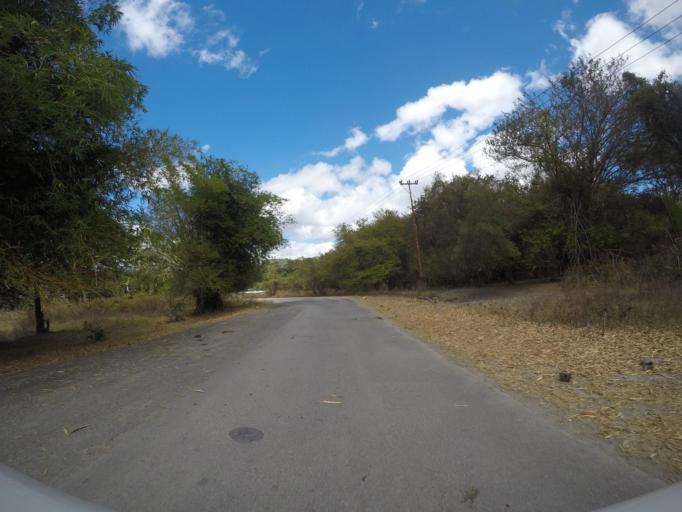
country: TL
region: Lautem
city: Lospalos
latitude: -8.4684
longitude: 126.8179
